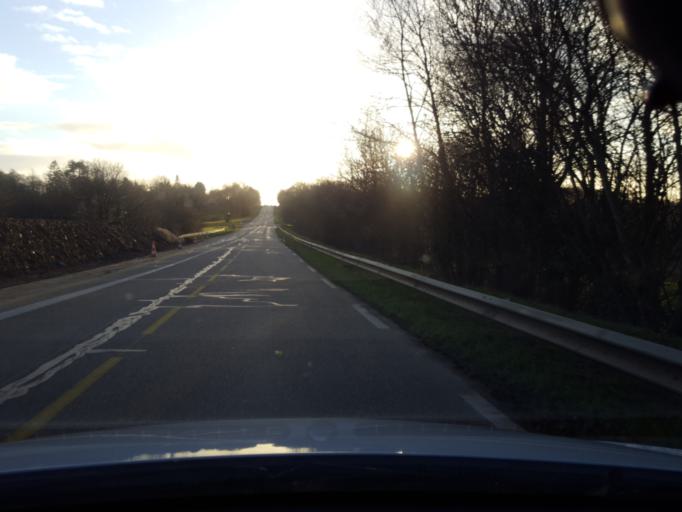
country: FR
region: Brittany
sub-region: Departement d'Ille-et-Vilaine
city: Guignen
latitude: 47.9380
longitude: -1.8416
